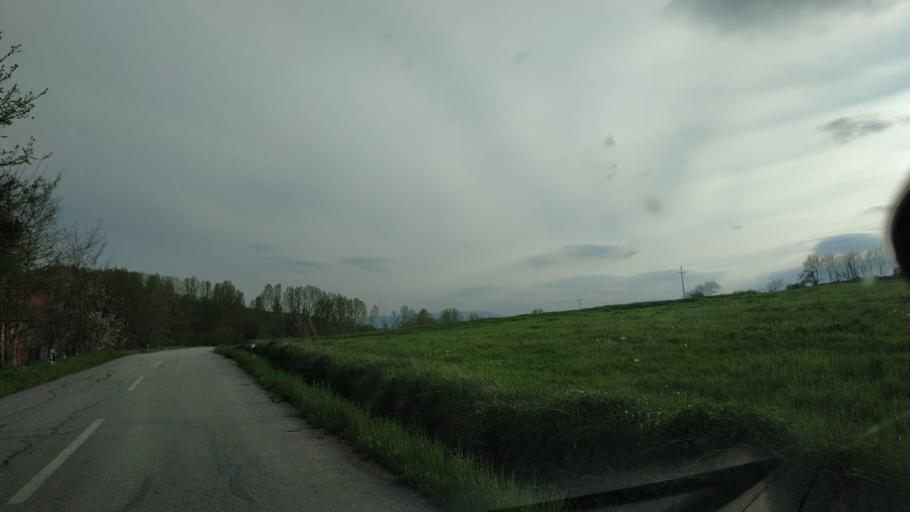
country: RS
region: Central Serbia
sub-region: Nisavski Okrug
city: Aleksinac
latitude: 43.5037
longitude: 21.8395
